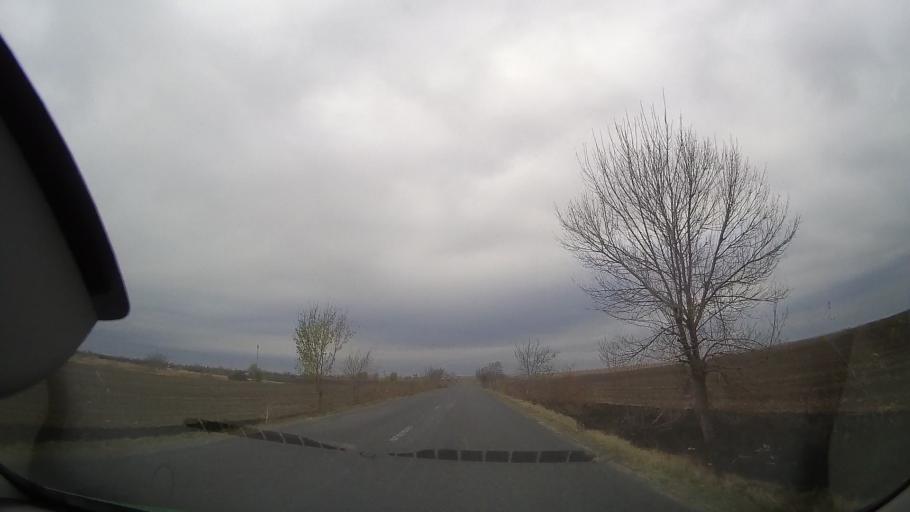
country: RO
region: Buzau
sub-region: Comuna Padina
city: Padina
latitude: 44.7826
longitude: 27.1506
